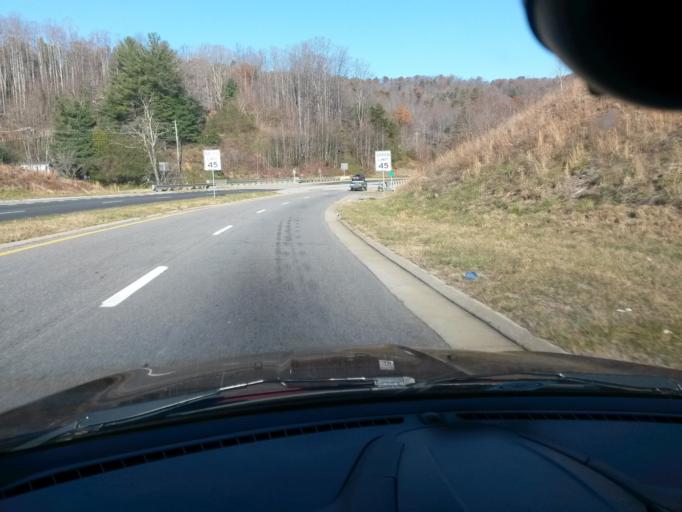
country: US
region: Virginia
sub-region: Patrick County
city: Stuart
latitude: 36.6503
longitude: -80.2843
